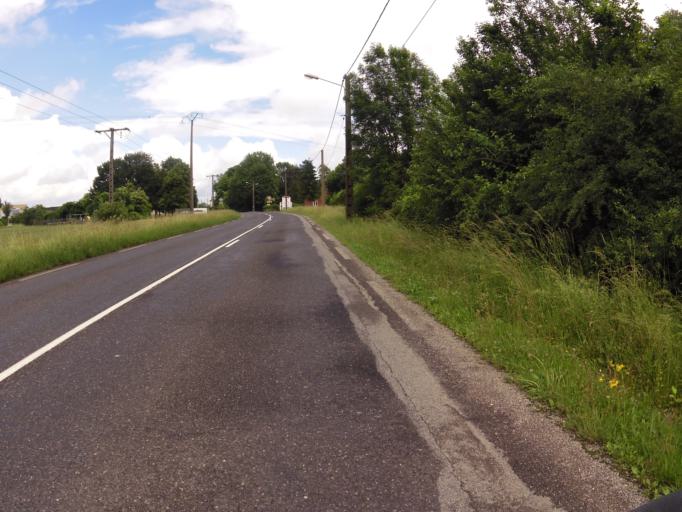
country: FR
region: Lorraine
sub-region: Departement de la Meuse
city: Revigny-sur-Ornain
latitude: 48.8159
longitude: 4.9763
